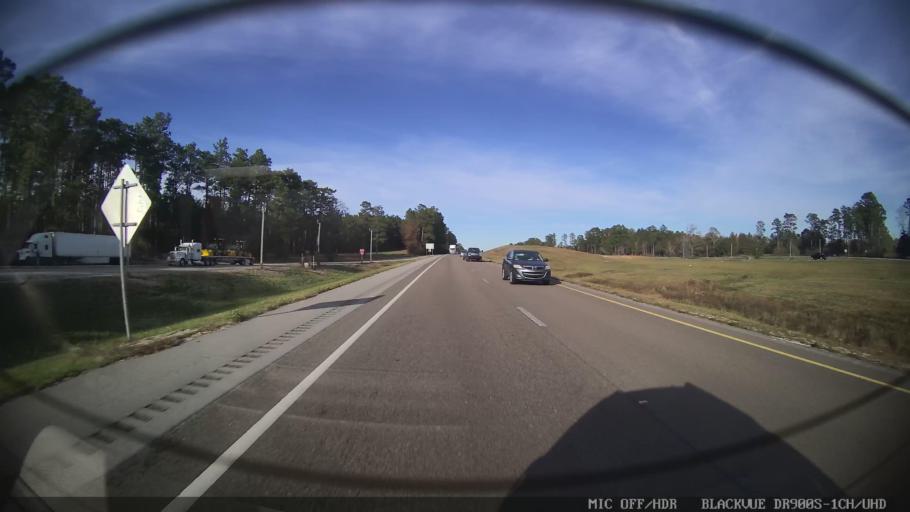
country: US
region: Mississippi
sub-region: Lamar County
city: Purvis
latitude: 31.2005
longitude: -89.3384
